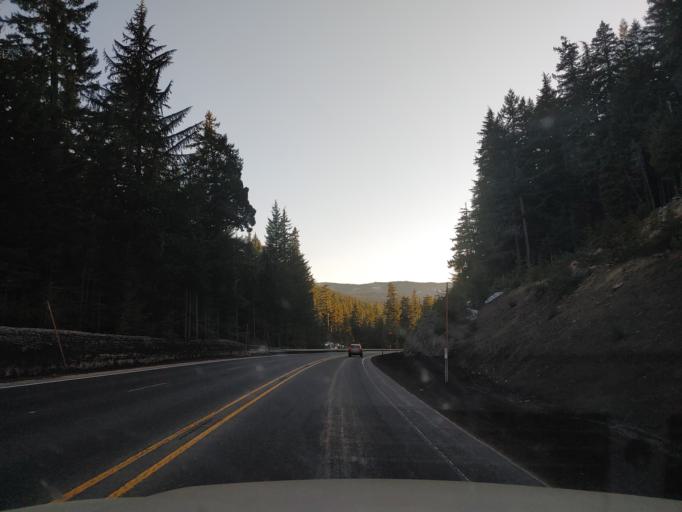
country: US
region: Oregon
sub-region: Lane County
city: Oakridge
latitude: 43.6133
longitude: -122.1048
